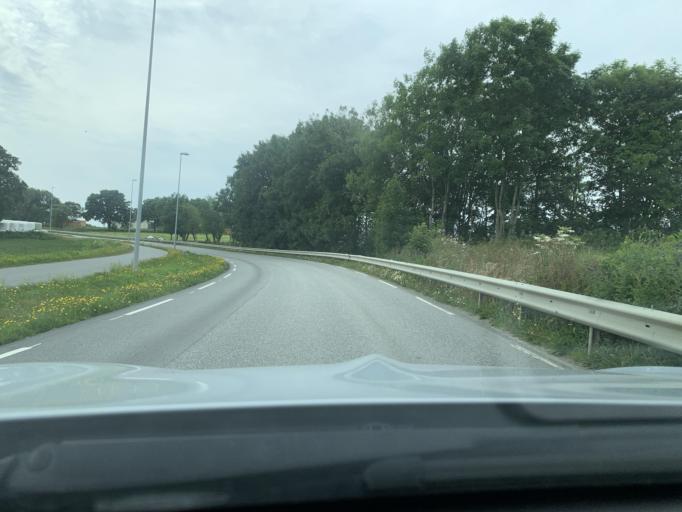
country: NO
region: Rogaland
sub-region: Time
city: Bryne
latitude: 58.7398
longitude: 5.6878
